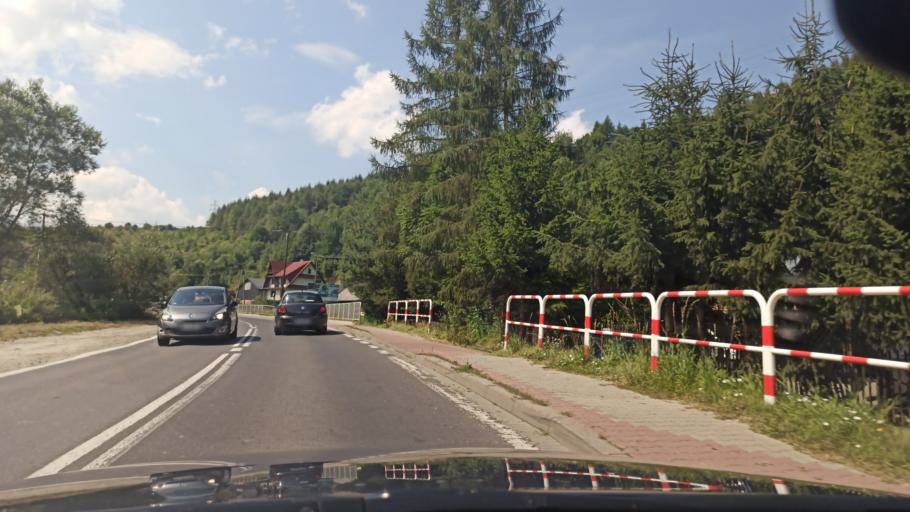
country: PL
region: Lesser Poland Voivodeship
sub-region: Powiat nowotarski
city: Kroscienko nad Dunajcem
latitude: 49.4391
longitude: 20.3881
